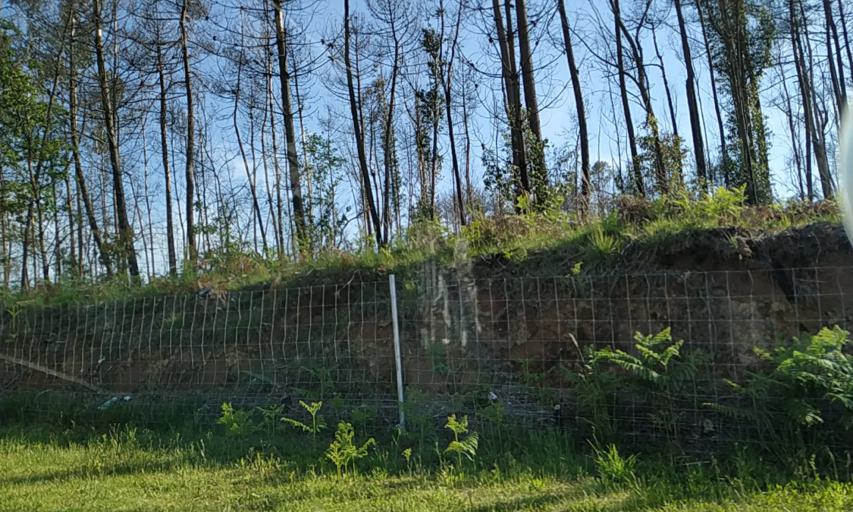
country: ES
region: Galicia
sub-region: Provincia de Pontevedra
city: Ponteareas
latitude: 42.1443
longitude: -8.4745
